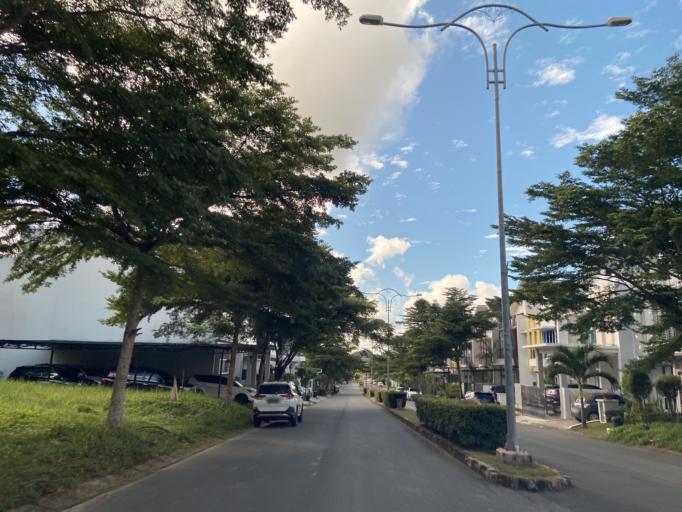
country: SG
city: Singapore
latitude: 1.0920
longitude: 104.0285
